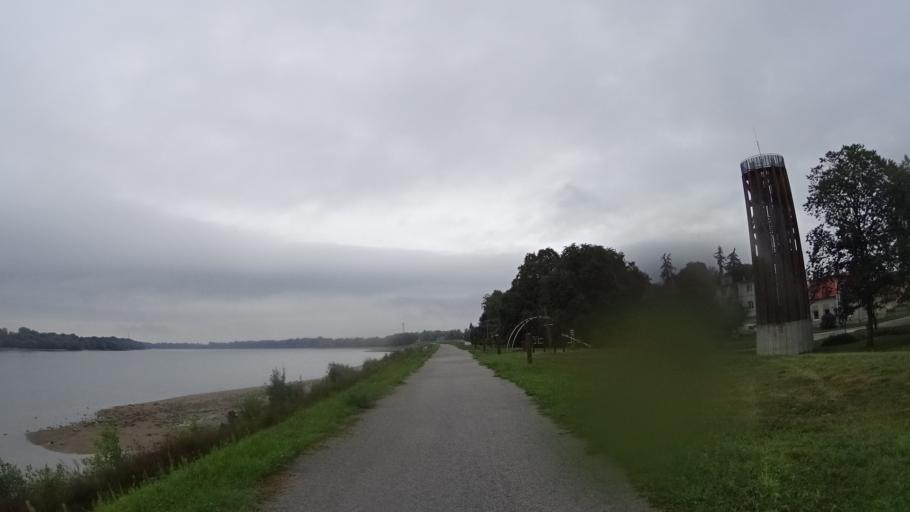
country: HU
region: Komarom-Esztergom
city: Labatlan
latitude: 47.7606
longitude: 18.4811
